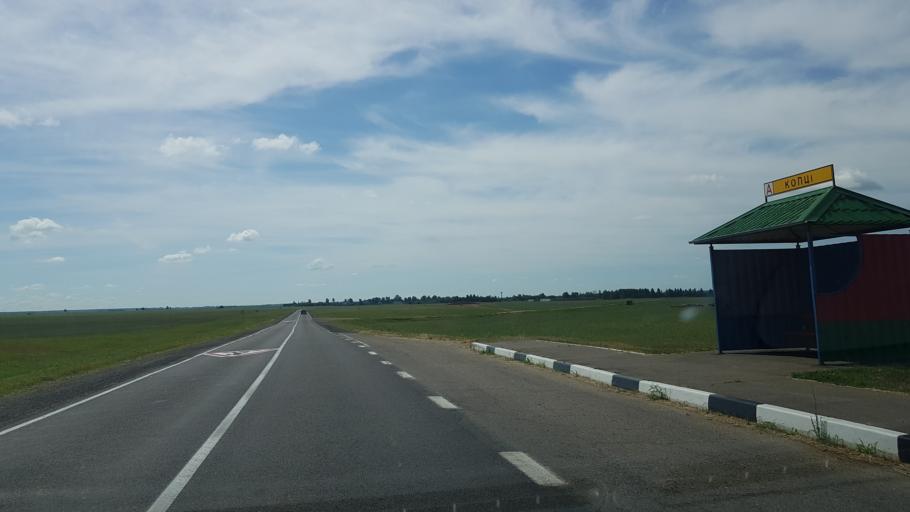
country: BY
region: Vitebsk
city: Dubrowna
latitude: 54.6303
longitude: 30.6640
